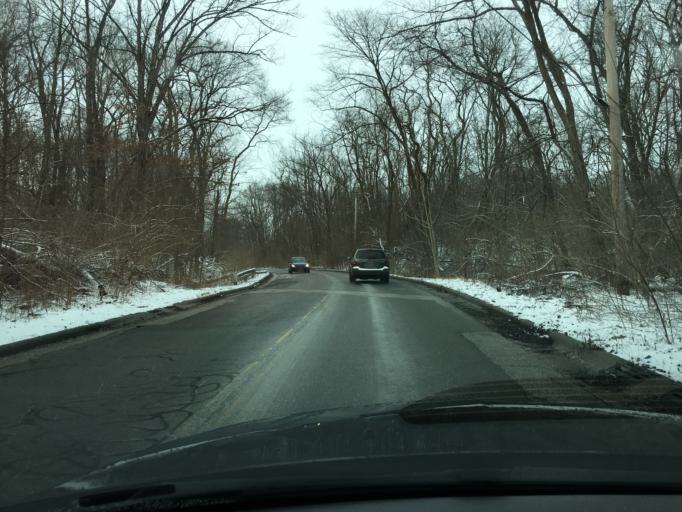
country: US
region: Ohio
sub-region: Summit County
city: Fairlawn
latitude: 41.1412
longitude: -81.5676
